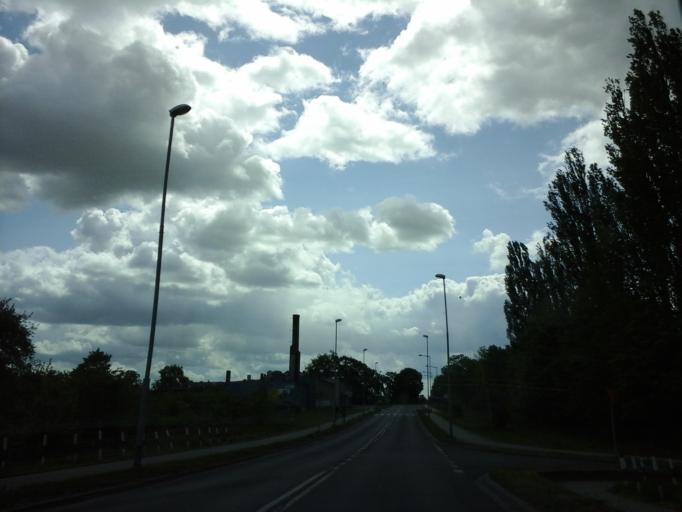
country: PL
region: West Pomeranian Voivodeship
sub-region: Powiat choszczenski
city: Choszczno
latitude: 53.1651
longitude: 15.4007
